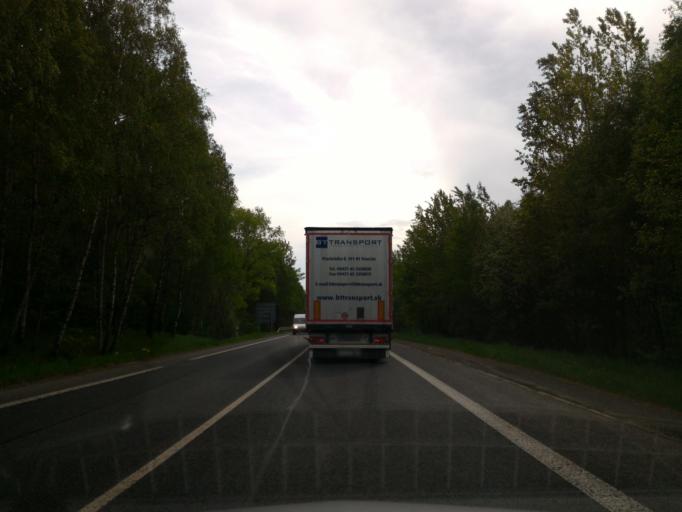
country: CZ
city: Cvikov
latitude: 50.7877
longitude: 14.5940
